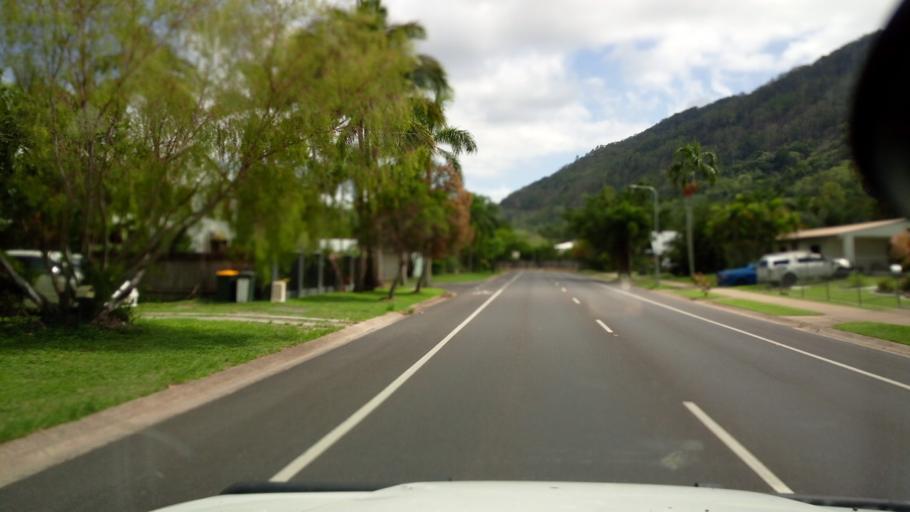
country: AU
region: Queensland
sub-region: Cairns
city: Redlynch
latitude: -16.9162
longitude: 145.7211
